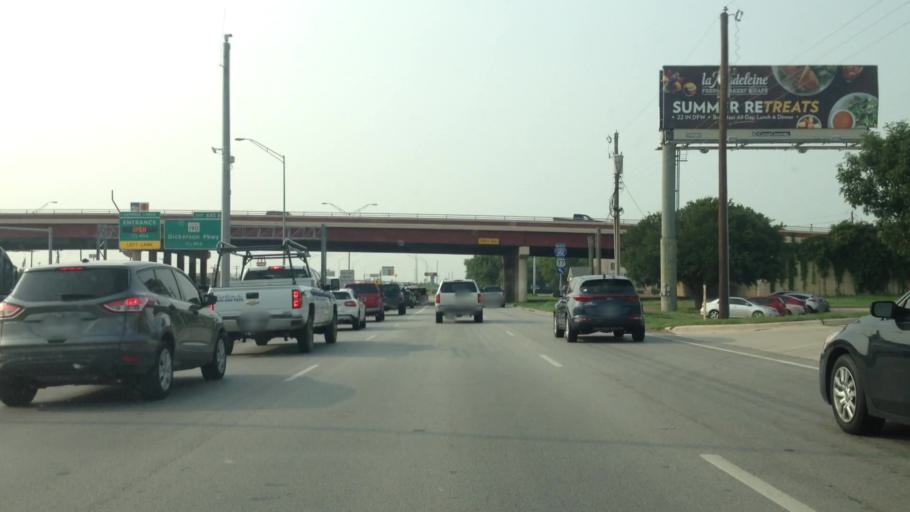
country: US
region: Texas
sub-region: Dallas County
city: Carrollton
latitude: 32.9634
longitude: -96.9163
